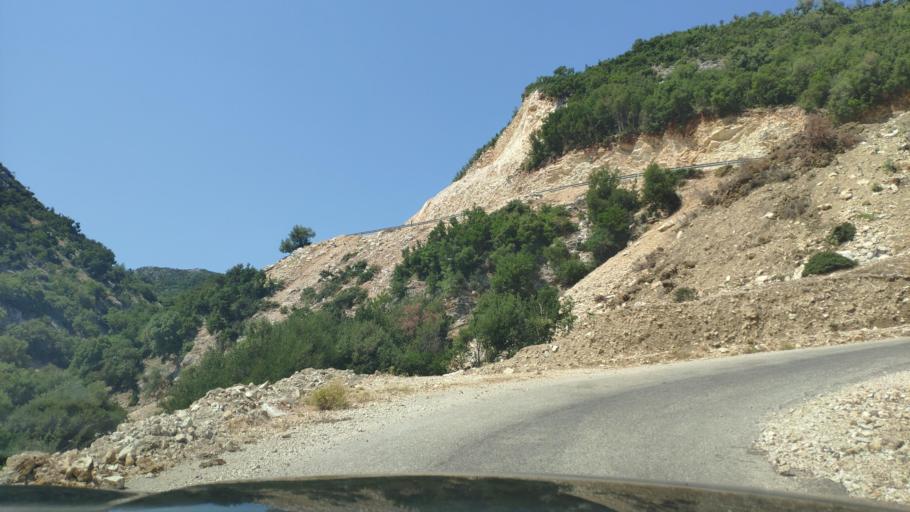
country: GR
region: West Greece
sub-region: Nomos Aitolias kai Akarnanias
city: Monastirakion
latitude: 38.8305
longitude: 20.9302
